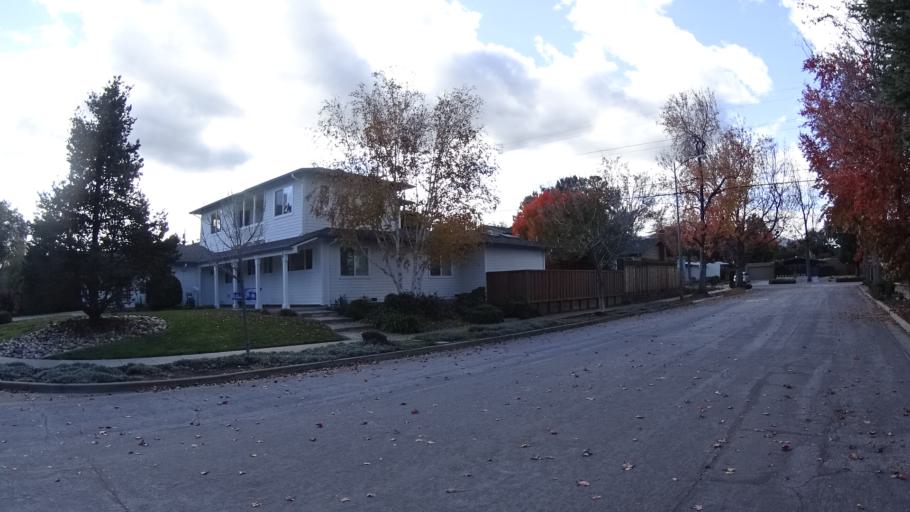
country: US
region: California
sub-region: Santa Clara County
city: Cupertino
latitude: 37.3392
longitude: -122.0541
